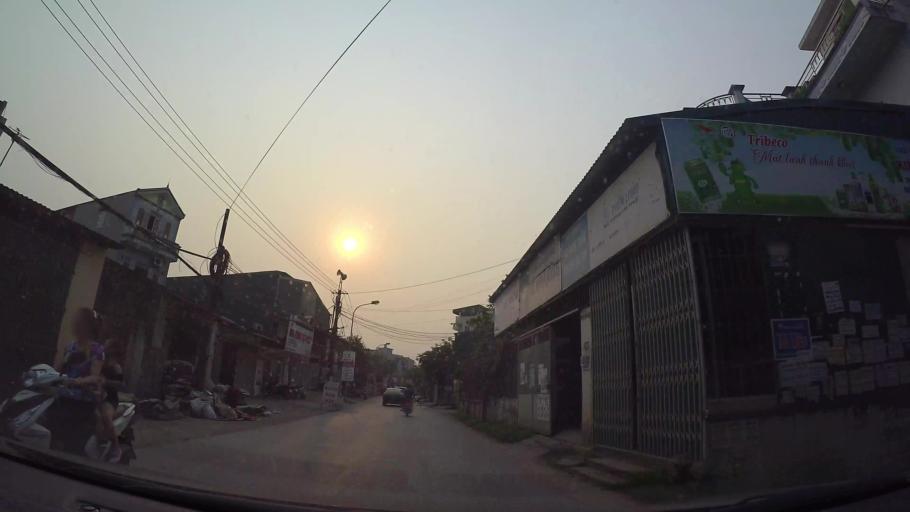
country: VN
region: Ha Noi
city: Kim Bai
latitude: 20.8683
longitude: 105.8087
